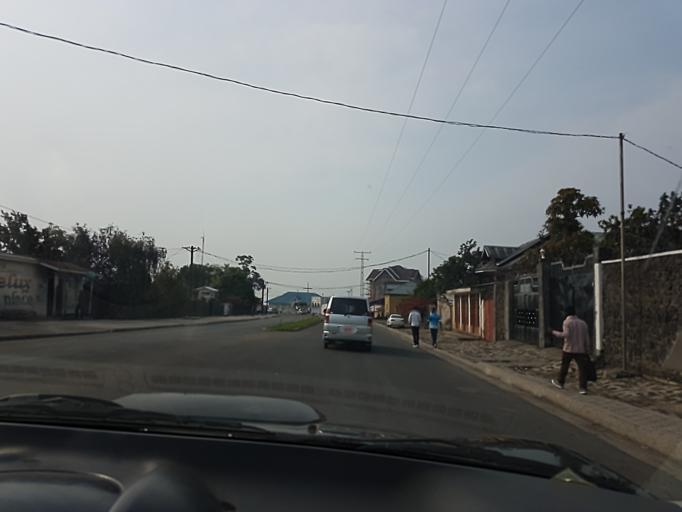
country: CD
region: Nord Kivu
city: Goma
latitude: -1.6854
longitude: 29.2285
